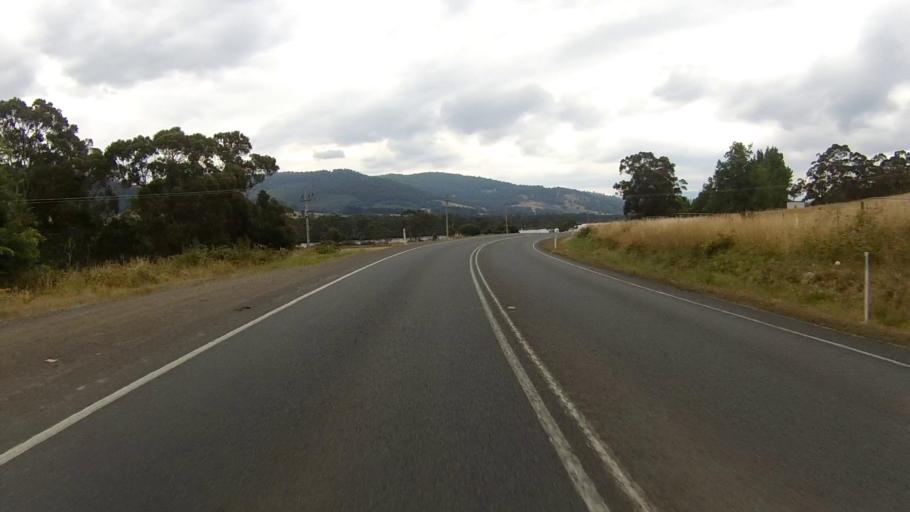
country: AU
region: Tasmania
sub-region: Huon Valley
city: Franklin
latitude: -43.0871
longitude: 147.0296
